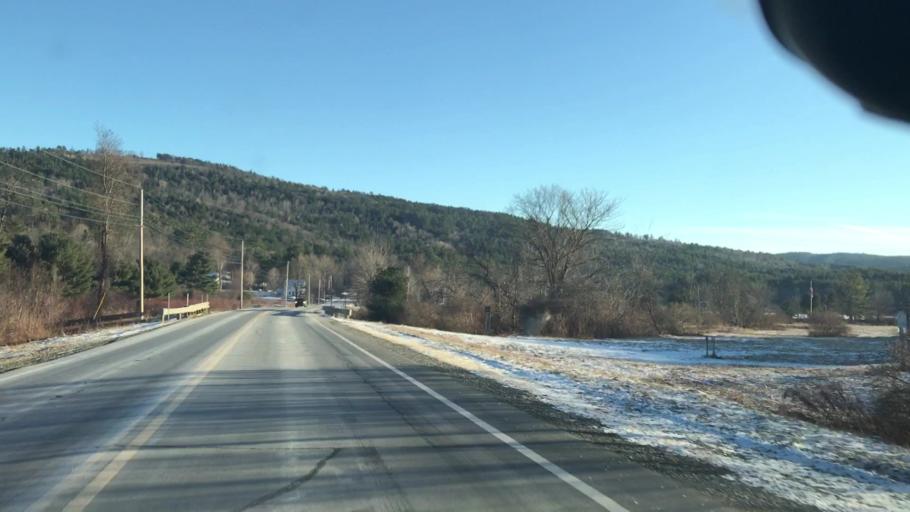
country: US
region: New Hampshire
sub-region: Grafton County
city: Lyme Town Offices
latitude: 43.8336
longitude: -72.1471
